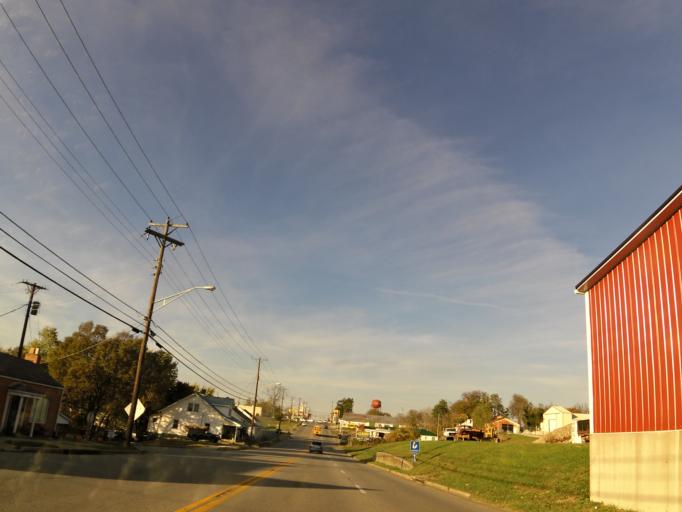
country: US
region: Kentucky
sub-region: Garrard County
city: Lancaster
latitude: 37.6129
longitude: -84.5798
